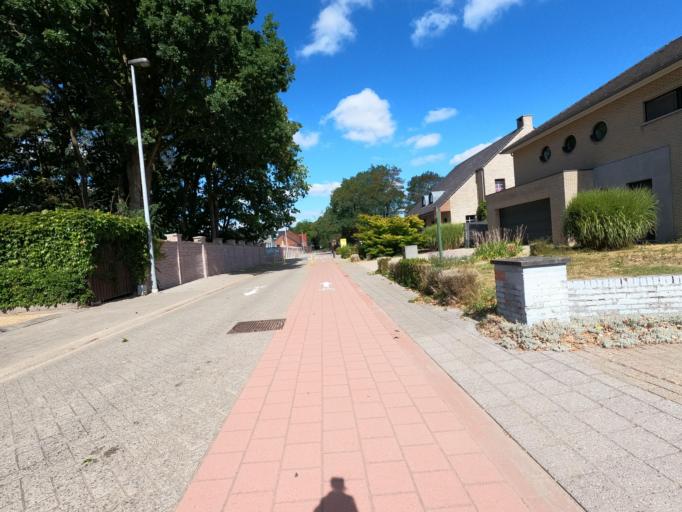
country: BE
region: Flanders
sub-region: Provincie Antwerpen
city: Hulshout
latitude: 51.0857
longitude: 4.8379
